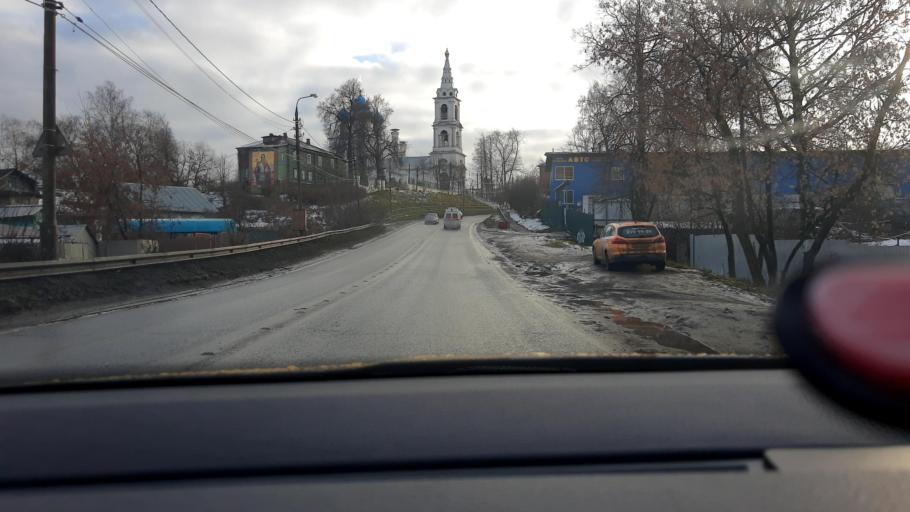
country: RU
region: Moskovskaya
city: Lesnyye Polyany
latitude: 55.9904
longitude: 37.8676
